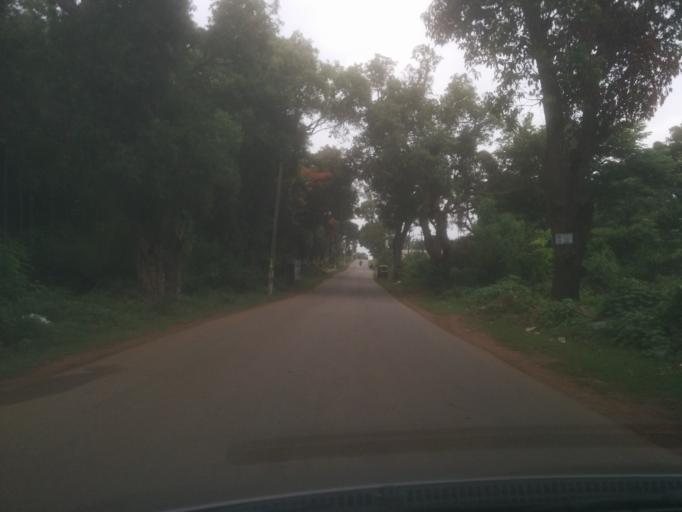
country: IN
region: Karnataka
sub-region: Chikmagalur
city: Chikmagalur
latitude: 13.3474
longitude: 75.7655
